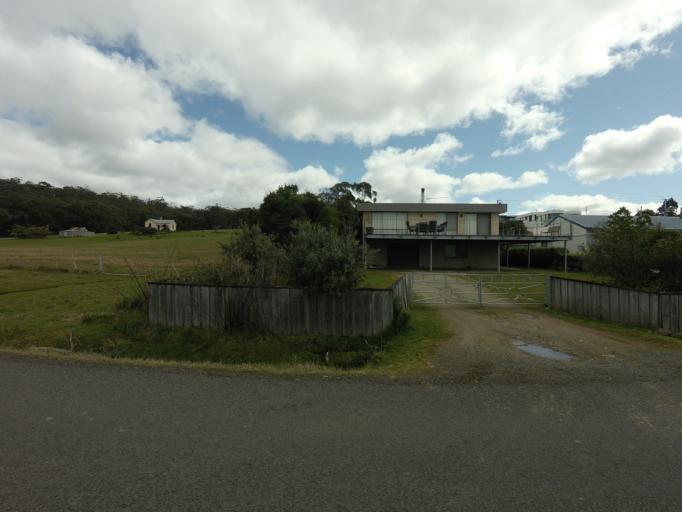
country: AU
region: Tasmania
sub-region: Huon Valley
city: Geeveston
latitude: -43.4401
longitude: 146.9612
